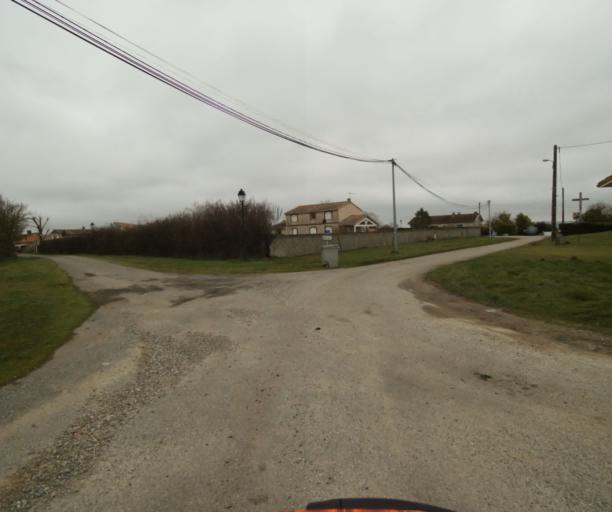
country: FR
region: Midi-Pyrenees
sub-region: Departement de la Haute-Garonne
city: Gaillac-Toulza
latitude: 43.2602
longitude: 1.5168
